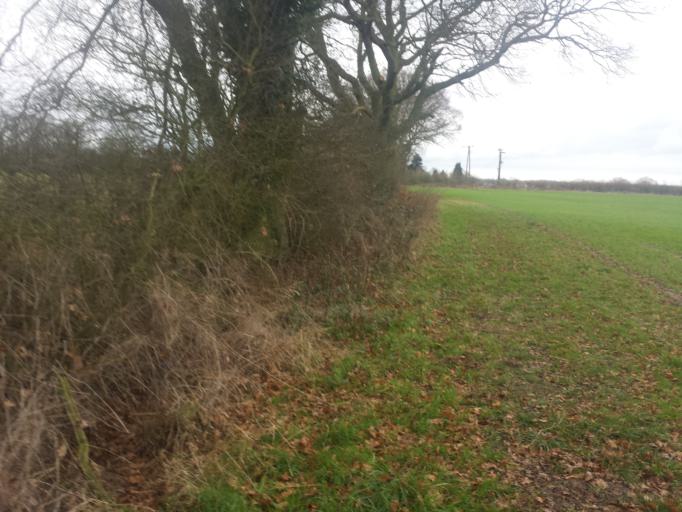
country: GB
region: England
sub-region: Essex
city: Great Bentley
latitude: 51.8890
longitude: 1.0414
